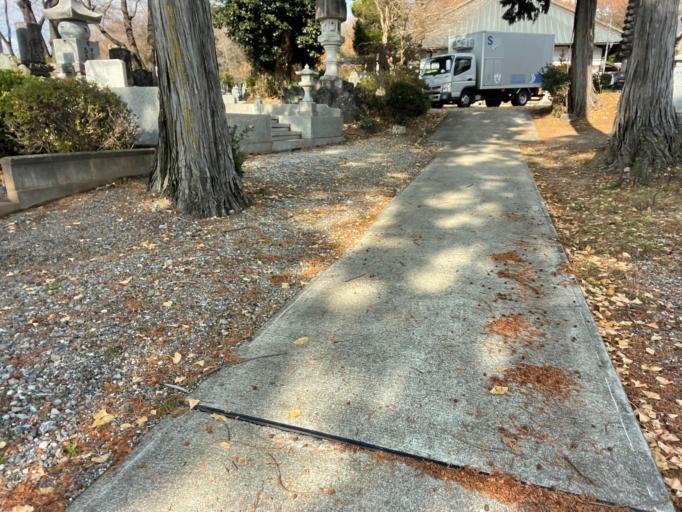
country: JP
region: Saitama
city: Yorii
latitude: 36.1577
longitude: 139.1885
